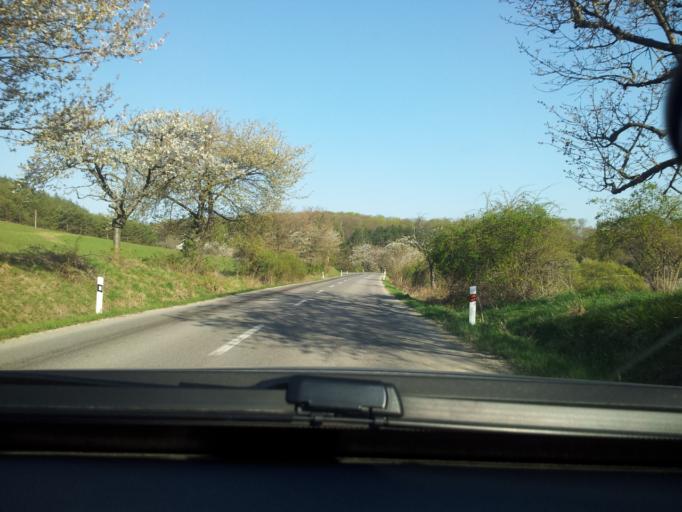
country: SK
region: Nitriansky
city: Partizanske
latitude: 48.5095
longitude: 18.4161
